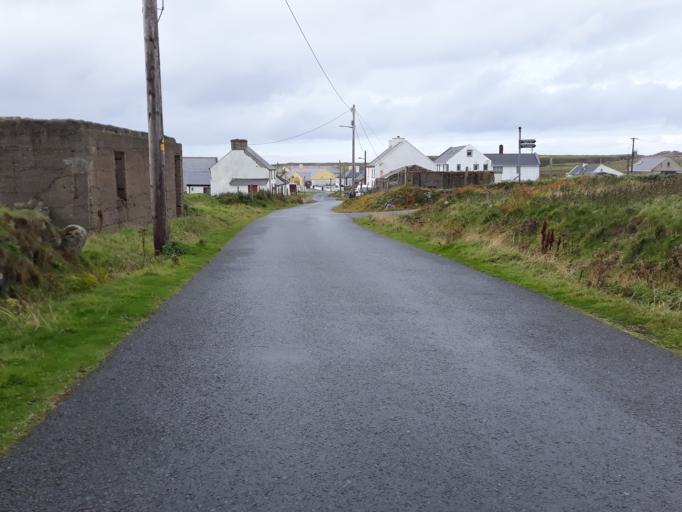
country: IE
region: Ulster
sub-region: County Donegal
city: Derrybeg
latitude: 55.2639
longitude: -8.2224
